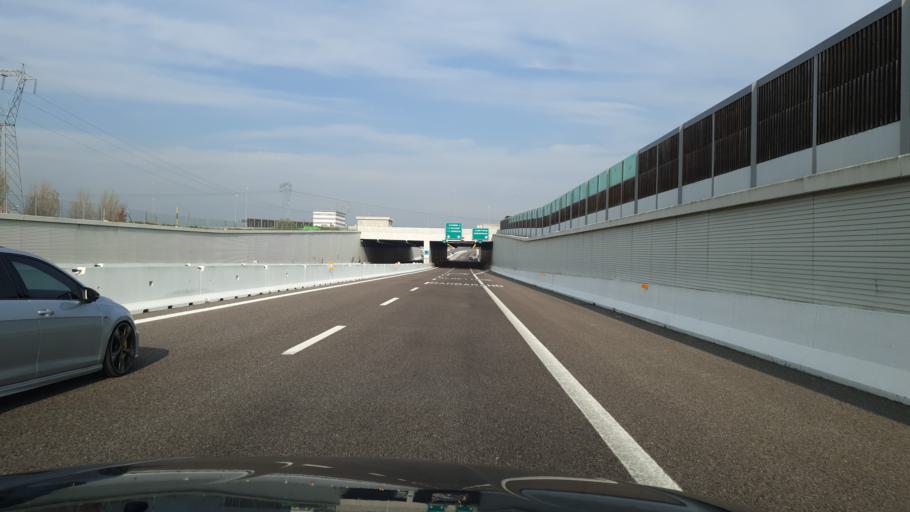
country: IT
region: Veneto
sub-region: Provincia di Vicenza
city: Albettone
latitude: 45.3779
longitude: 11.6112
